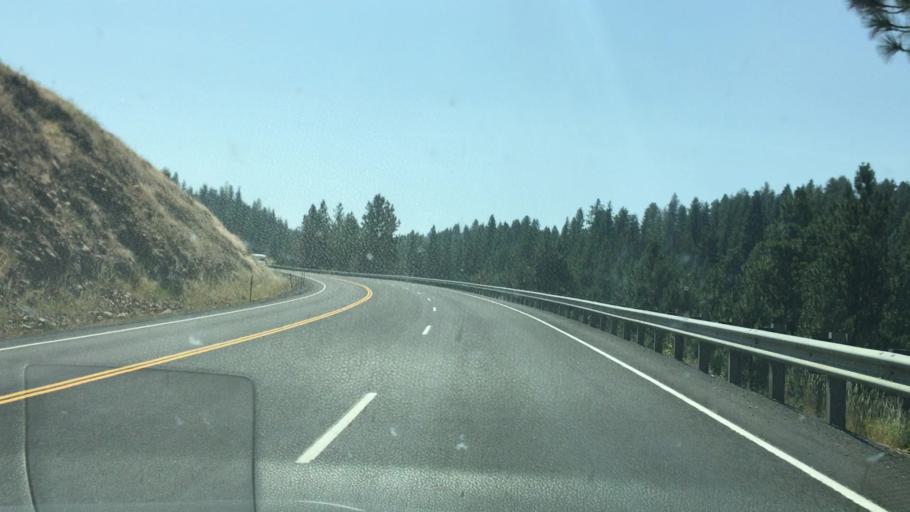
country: US
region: Idaho
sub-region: Idaho County
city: Grangeville
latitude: 45.8707
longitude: -116.2365
